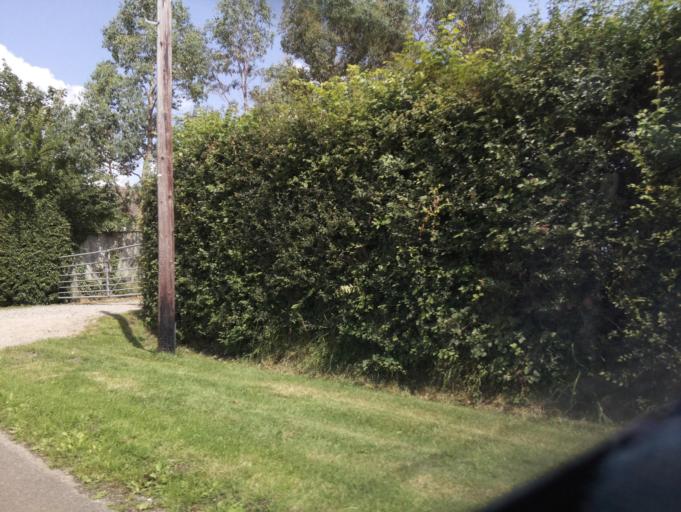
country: GB
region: England
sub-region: Wiltshire
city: Minety
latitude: 51.6033
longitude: -1.9475
